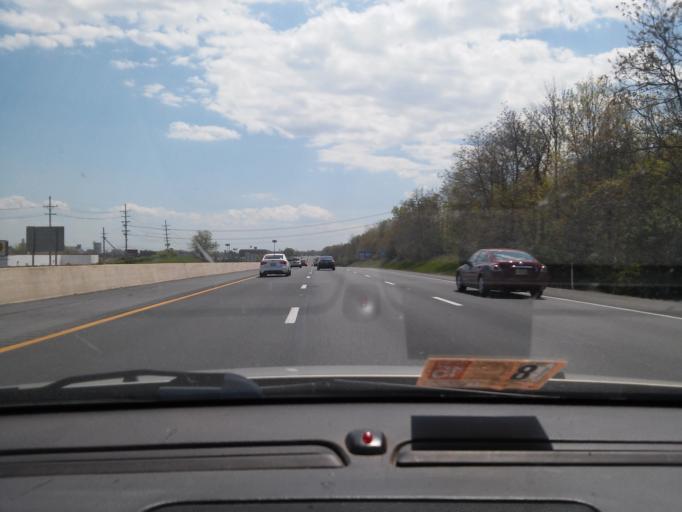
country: US
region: West Virginia
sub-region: Berkeley County
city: Martinsburg
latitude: 39.4578
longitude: -77.9900
